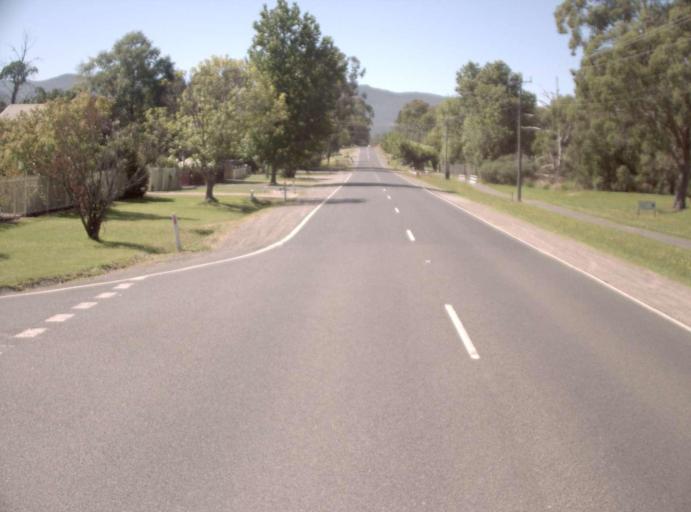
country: AU
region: Victoria
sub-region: Yarra Ranges
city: Healesville
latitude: -37.6561
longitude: 145.5269
